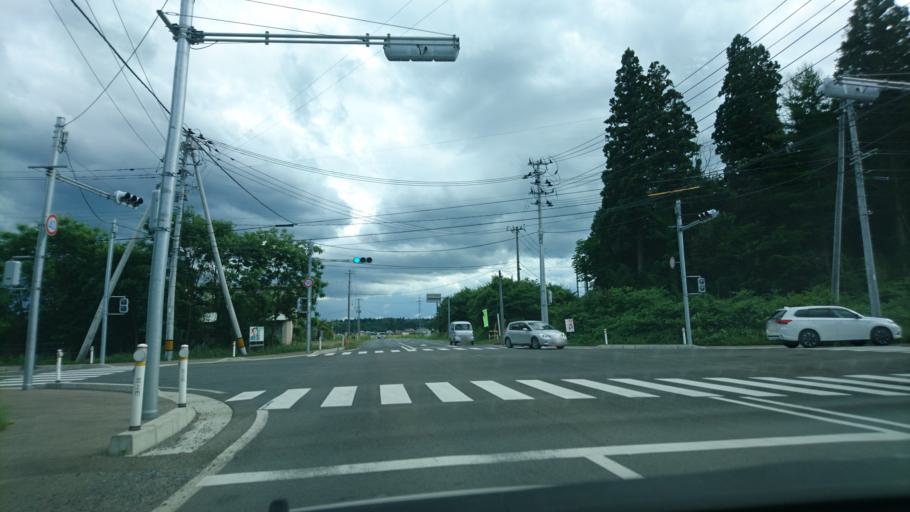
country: JP
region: Iwate
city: Kitakami
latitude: 39.3214
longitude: 141.1272
